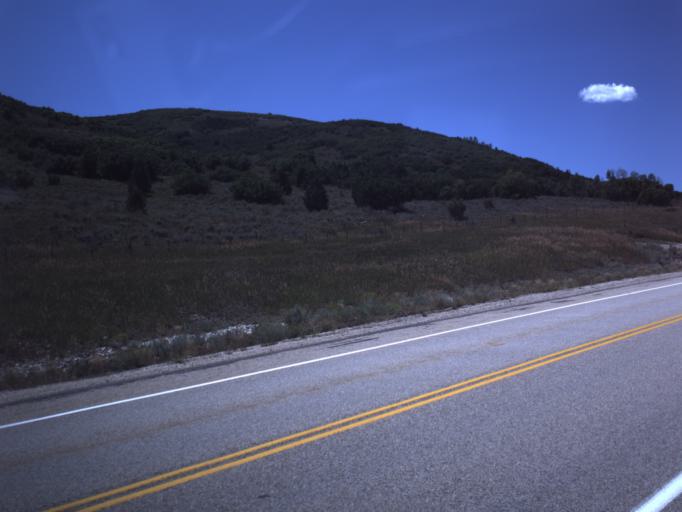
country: US
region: Utah
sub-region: Summit County
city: Francis
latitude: 40.5958
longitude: -111.3604
